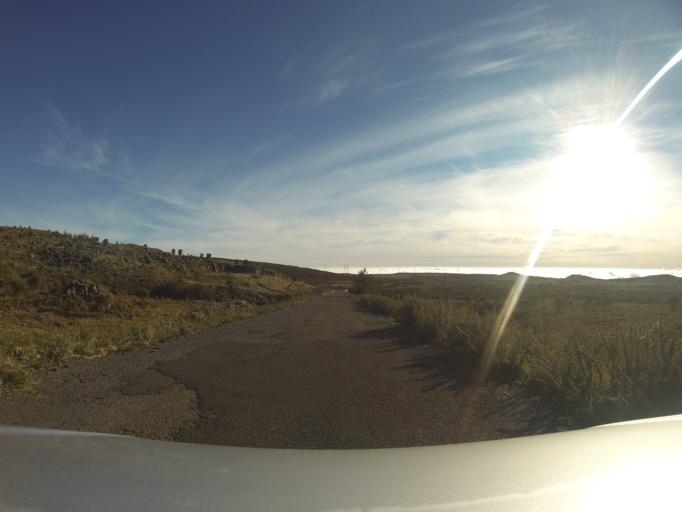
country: PT
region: Madeira
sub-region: Sao Vicente
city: Sao Vicente
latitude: 32.7646
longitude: -17.0820
